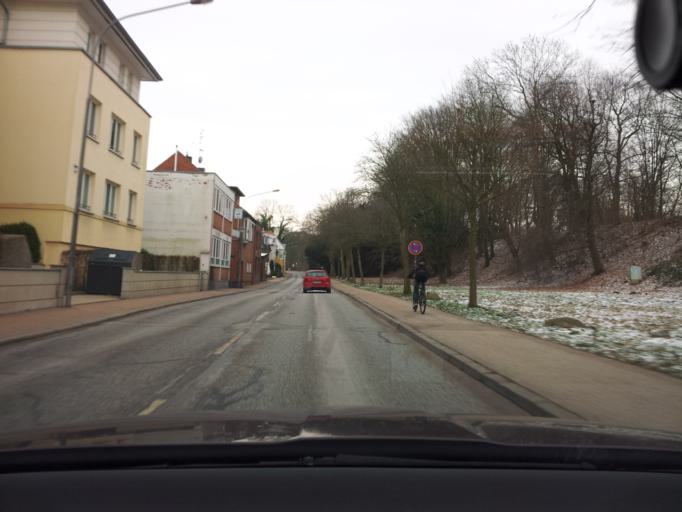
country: DE
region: Schleswig-Holstein
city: Luebeck
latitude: 53.8598
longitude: 10.6826
